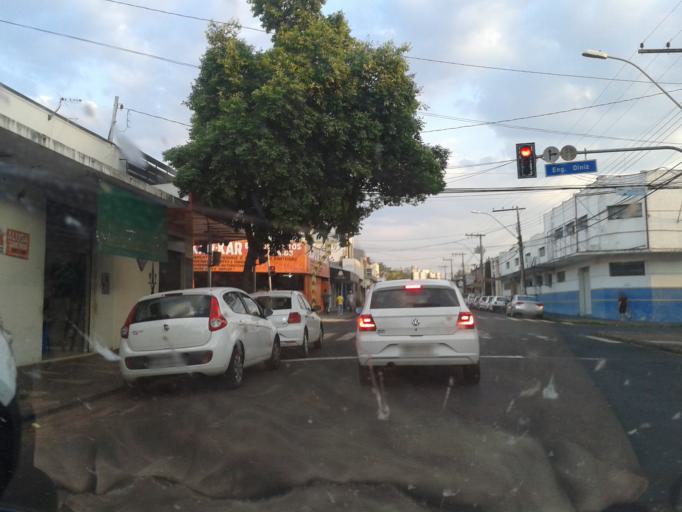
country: BR
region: Minas Gerais
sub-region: Uberlandia
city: Uberlandia
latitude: -18.9087
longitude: -48.2778
